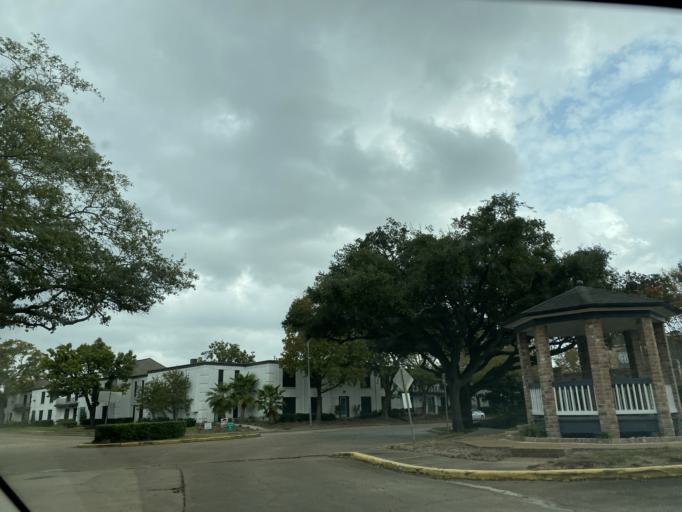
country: US
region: Texas
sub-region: Harris County
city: Piney Point Village
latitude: 29.7422
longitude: -95.4978
